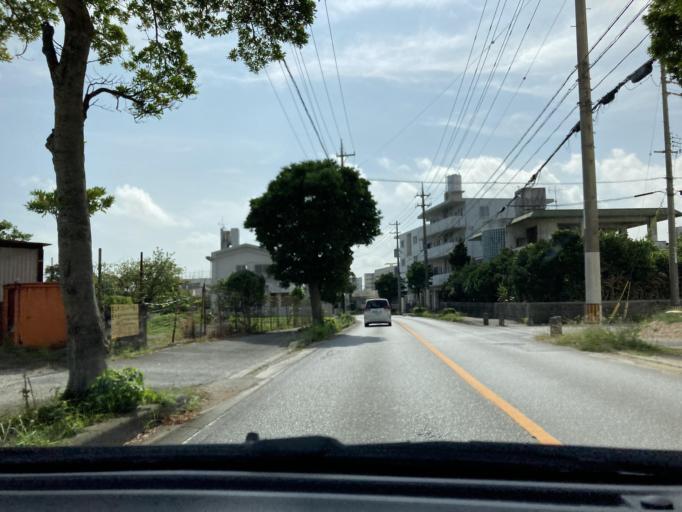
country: JP
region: Okinawa
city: Ginowan
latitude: 26.2552
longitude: 127.7721
